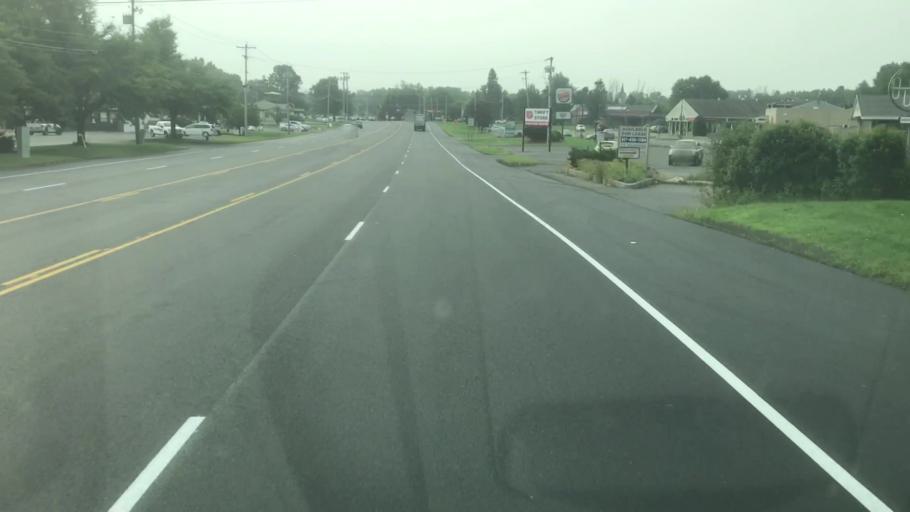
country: US
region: New York
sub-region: Onondaga County
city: Liverpool
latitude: 43.1389
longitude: -76.2269
